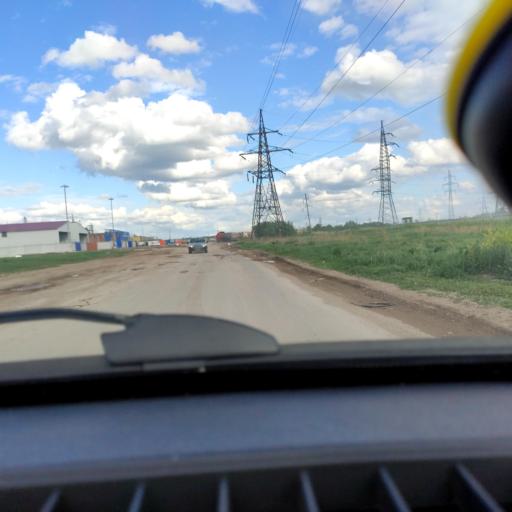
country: RU
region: Samara
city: Tol'yatti
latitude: 53.5476
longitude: 49.4685
